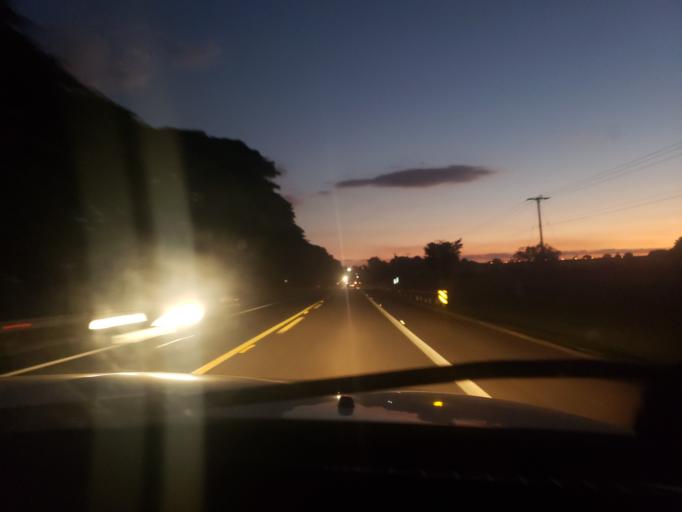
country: BR
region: Sao Paulo
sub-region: Conchal
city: Conchal
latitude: -22.3219
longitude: -47.1412
